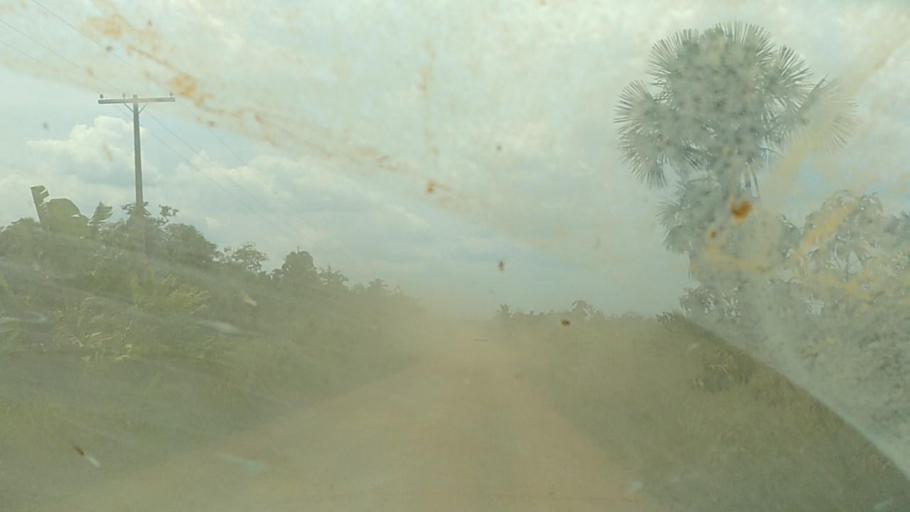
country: BR
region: Rondonia
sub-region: Porto Velho
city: Porto Velho
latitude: -8.9469
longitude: -64.3099
